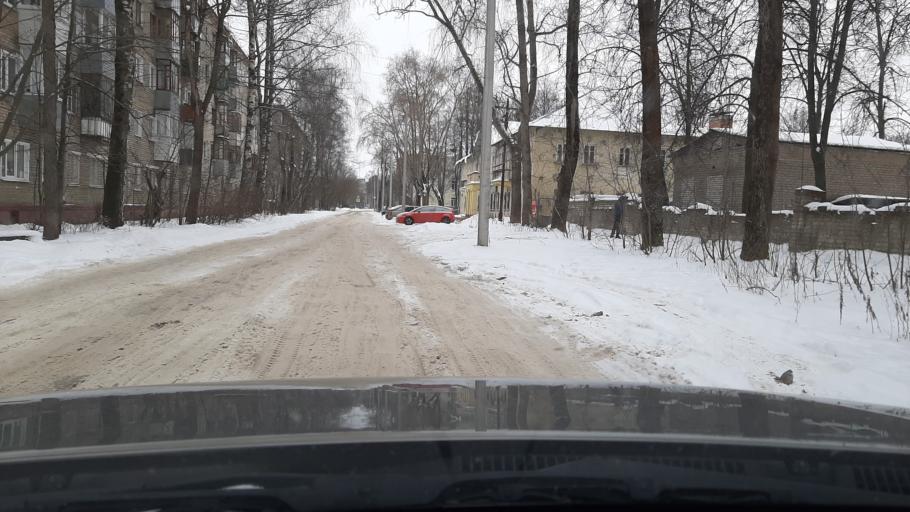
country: RU
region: Ivanovo
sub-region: Gorod Ivanovo
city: Ivanovo
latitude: 56.9712
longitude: 40.9681
